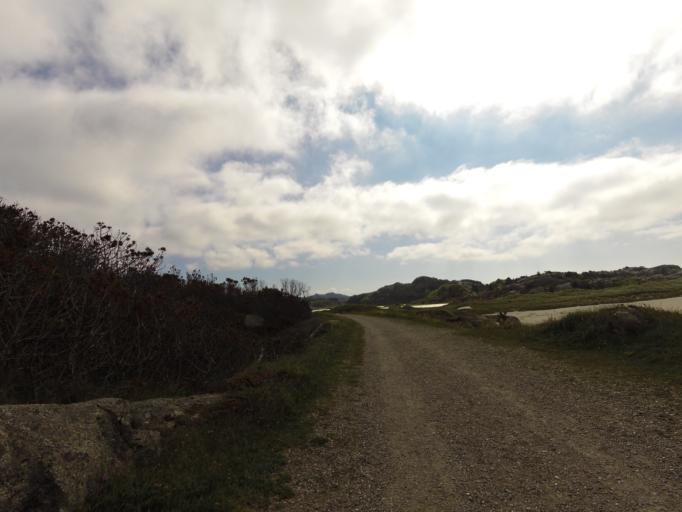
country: NO
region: Rogaland
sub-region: Ha
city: Vigrestad
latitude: 58.5254
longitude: 5.7782
